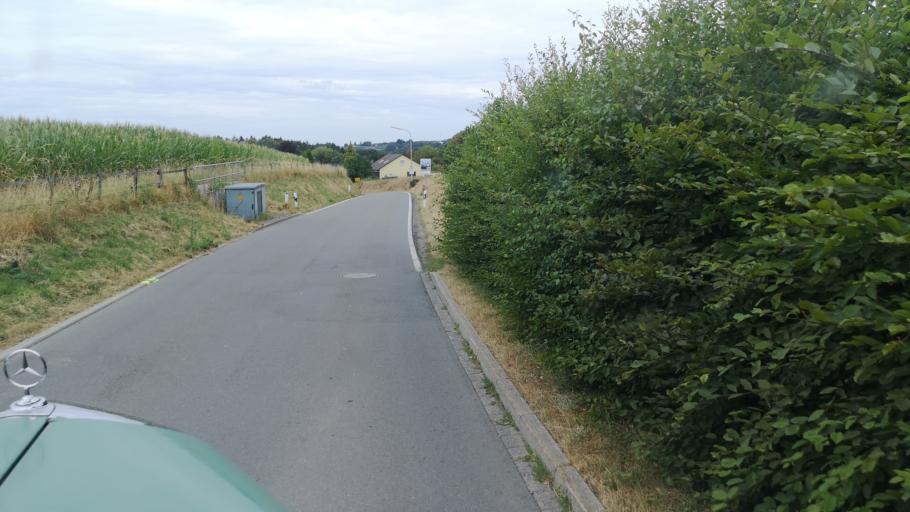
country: DE
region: North Rhine-Westphalia
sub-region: Regierungsbezirk Koln
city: Odenthal
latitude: 51.0585
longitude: 7.1558
